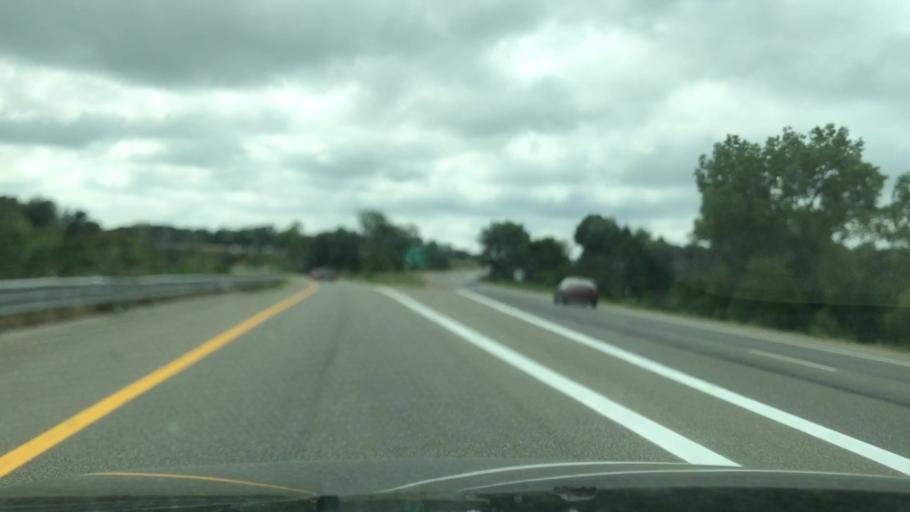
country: US
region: Michigan
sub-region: Muskegon County
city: Fruitport
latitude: 43.0738
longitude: -86.0772
